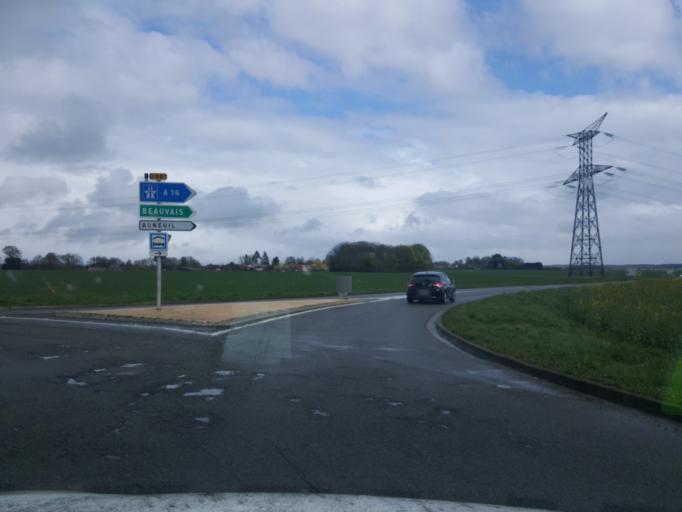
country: FR
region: Picardie
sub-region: Departement de l'Oise
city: Chaumont-en-Vexin
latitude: 49.3170
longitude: 1.8859
